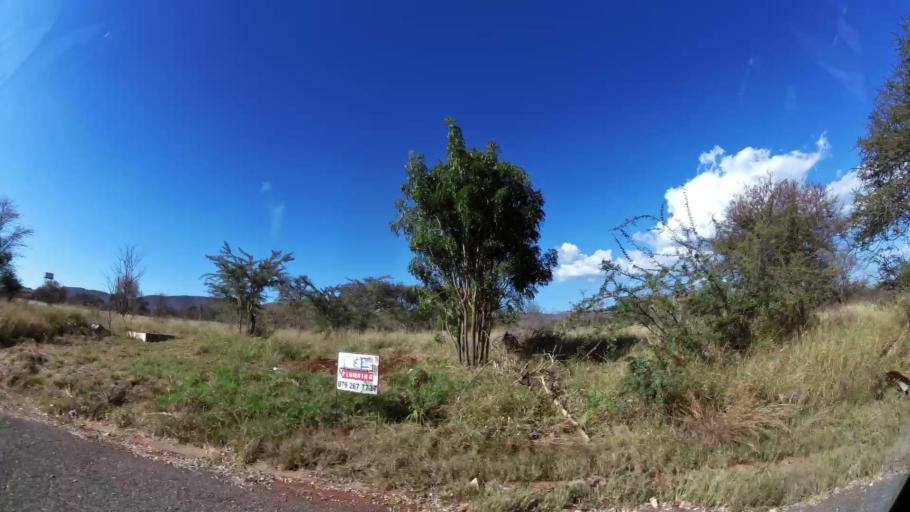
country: ZA
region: Limpopo
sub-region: Waterberg District Municipality
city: Mokopane
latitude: -24.2013
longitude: 29.0132
